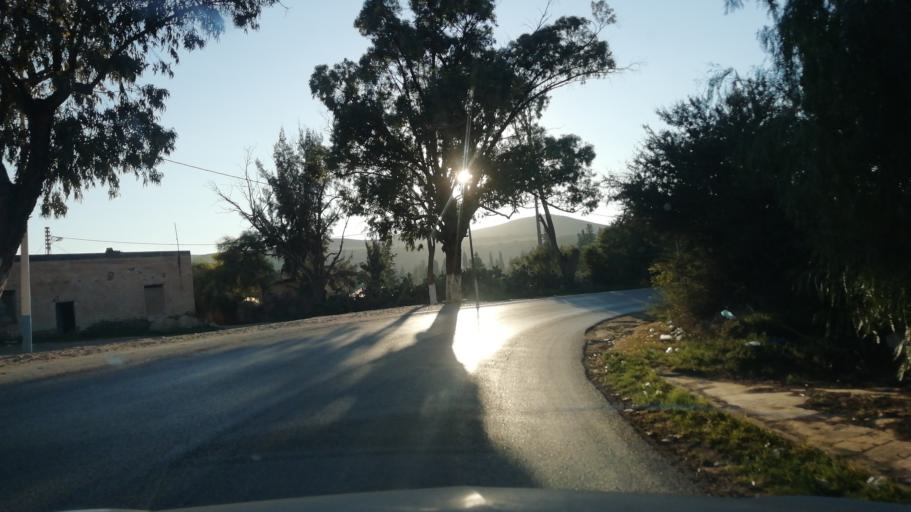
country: DZ
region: Tlemcen
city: Nedroma
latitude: 34.8255
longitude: -1.6509
